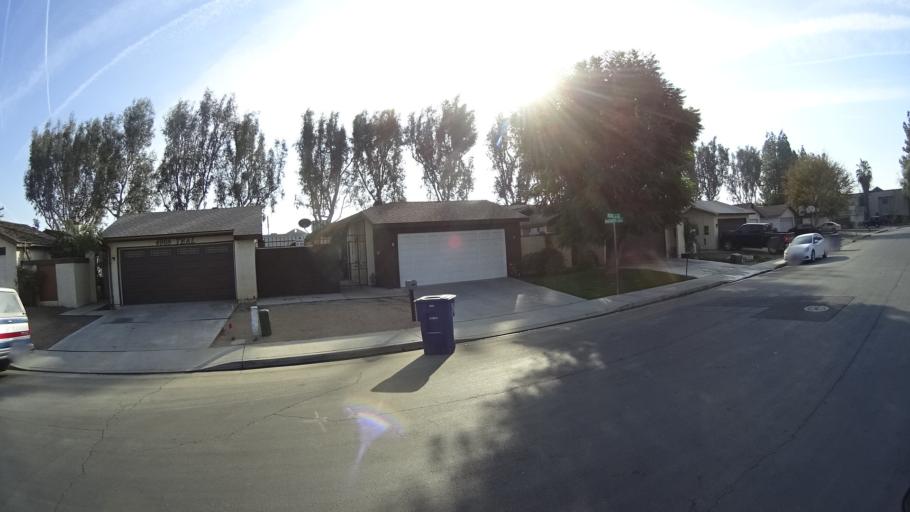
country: US
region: California
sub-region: Kern County
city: Bakersfield
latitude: 35.3199
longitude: -119.0260
